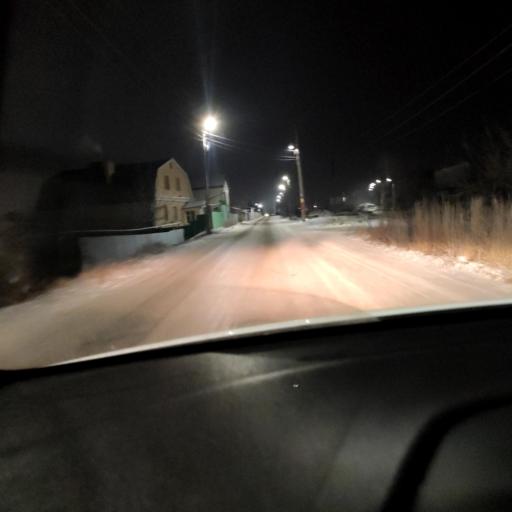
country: RU
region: Tatarstan
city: Staroye Arakchino
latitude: 55.8836
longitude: 49.0399
